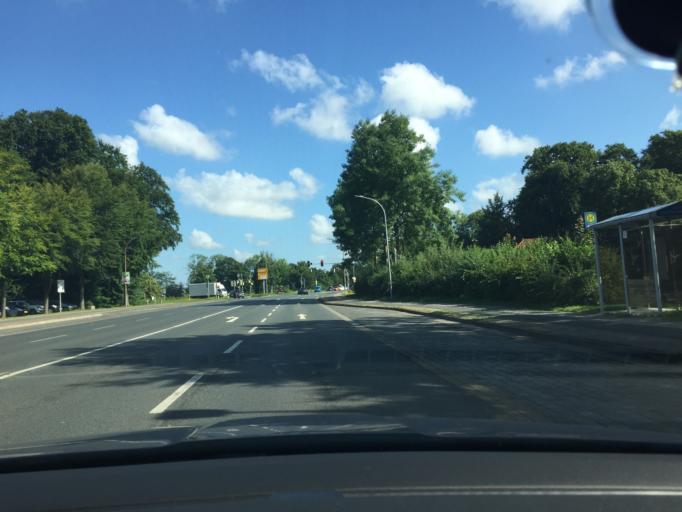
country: DE
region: Lower Saxony
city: Aurich
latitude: 53.4895
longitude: 7.4960
